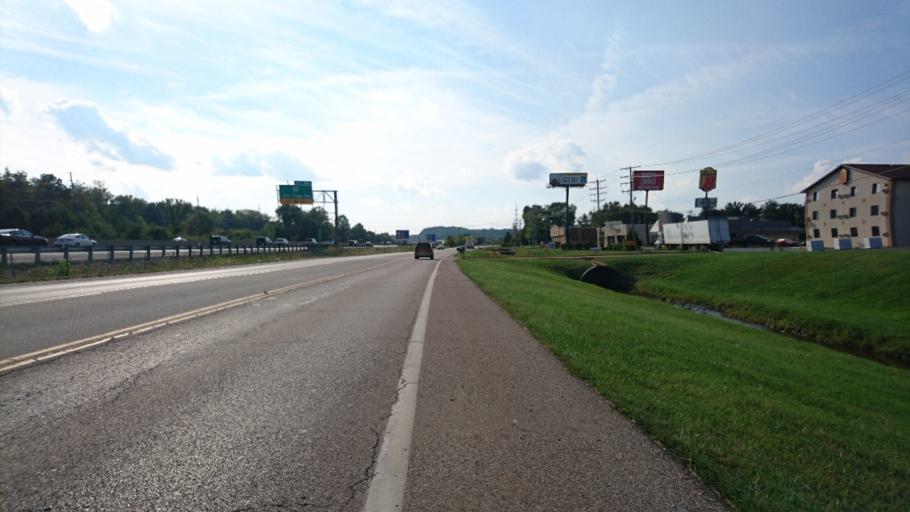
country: US
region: Missouri
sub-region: Saint Louis County
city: Eureka
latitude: 38.5047
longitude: -90.6643
